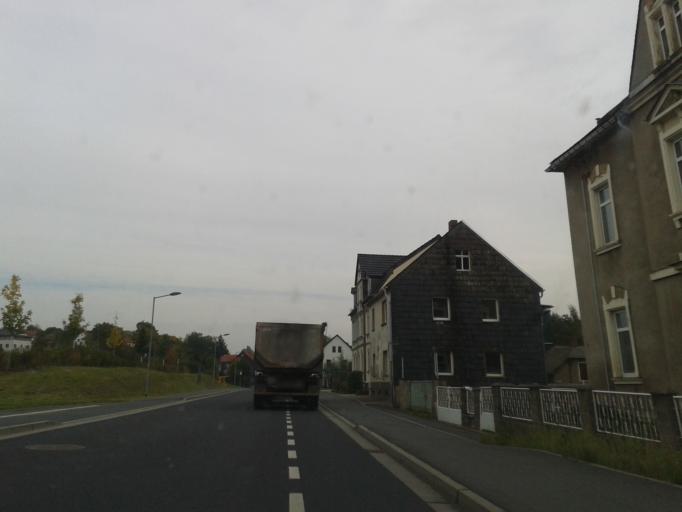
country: DE
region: Saxony
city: Nossen
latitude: 51.0580
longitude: 13.3126
